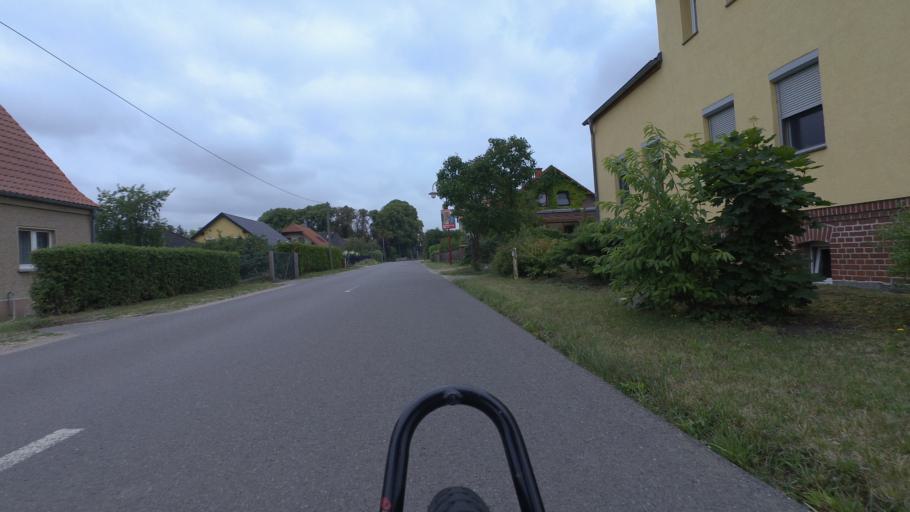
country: DE
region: Brandenburg
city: Beelitz
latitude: 52.2210
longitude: 12.9994
